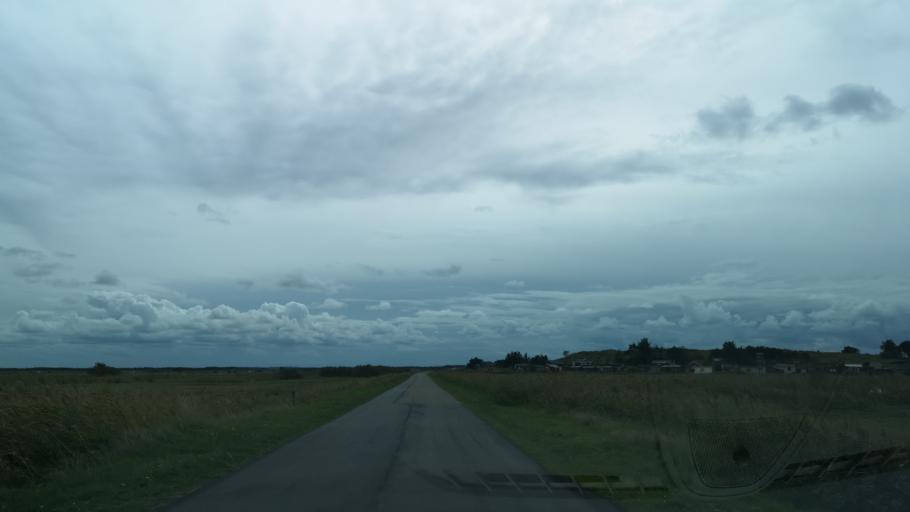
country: DK
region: Central Jutland
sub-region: Ringkobing-Skjern Kommune
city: Hvide Sande
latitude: 55.8549
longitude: 8.2200
